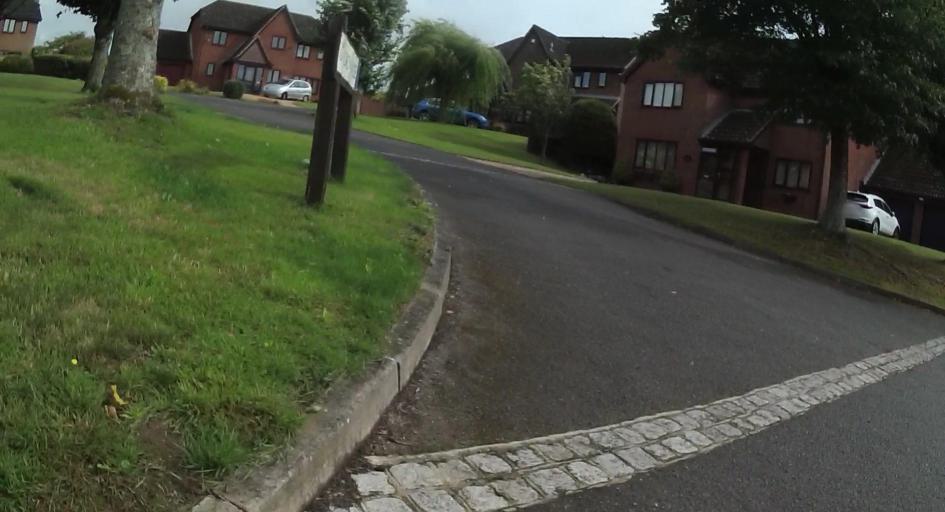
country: GB
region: England
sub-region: Hampshire
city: Andover
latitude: 51.2236
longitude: -1.4309
